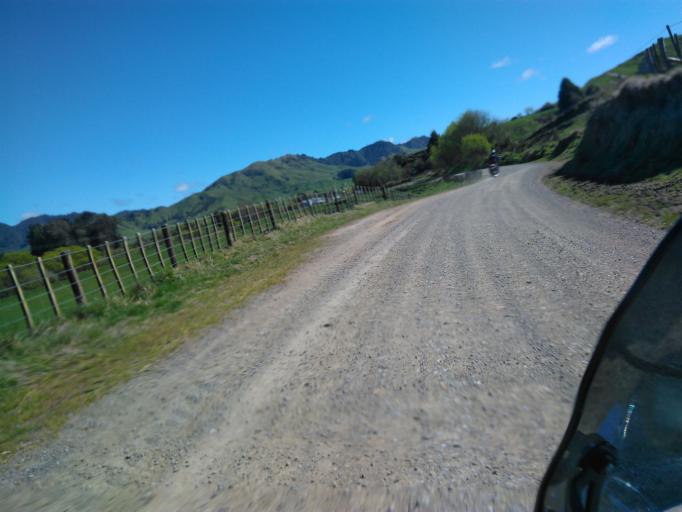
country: NZ
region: Bay of Plenty
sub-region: Opotiki District
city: Opotiki
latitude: -38.2842
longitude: 177.5424
